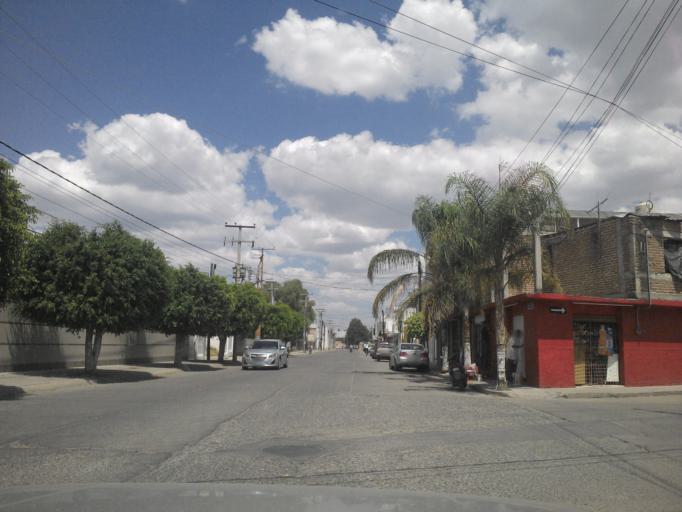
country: MX
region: Guanajuato
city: San Francisco del Rincon
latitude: 21.0239
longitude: -101.8683
